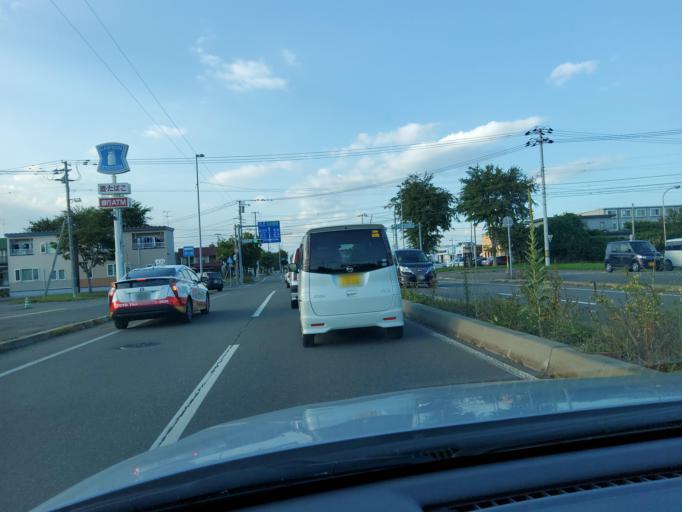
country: JP
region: Hokkaido
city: Obihiro
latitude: 42.9291
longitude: 143.1853
